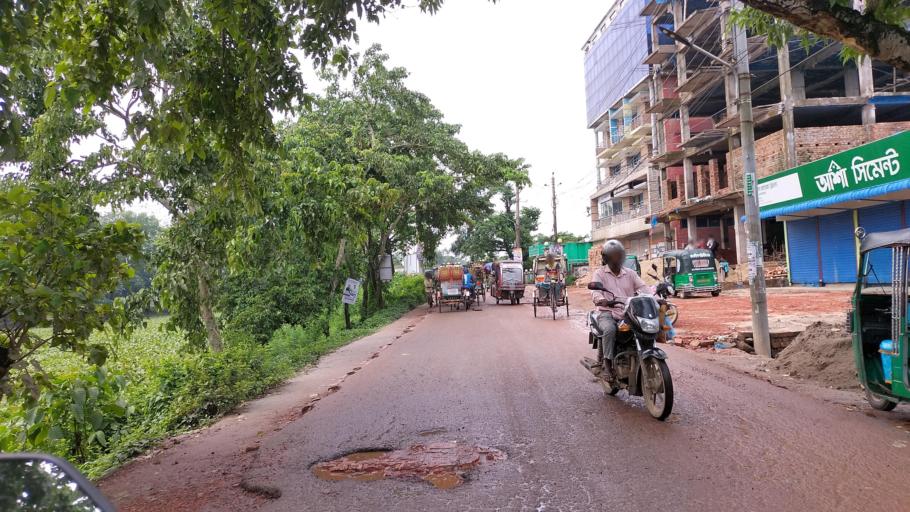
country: BD
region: Dhaka
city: Netrakona
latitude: 24.8918
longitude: 90.7389
